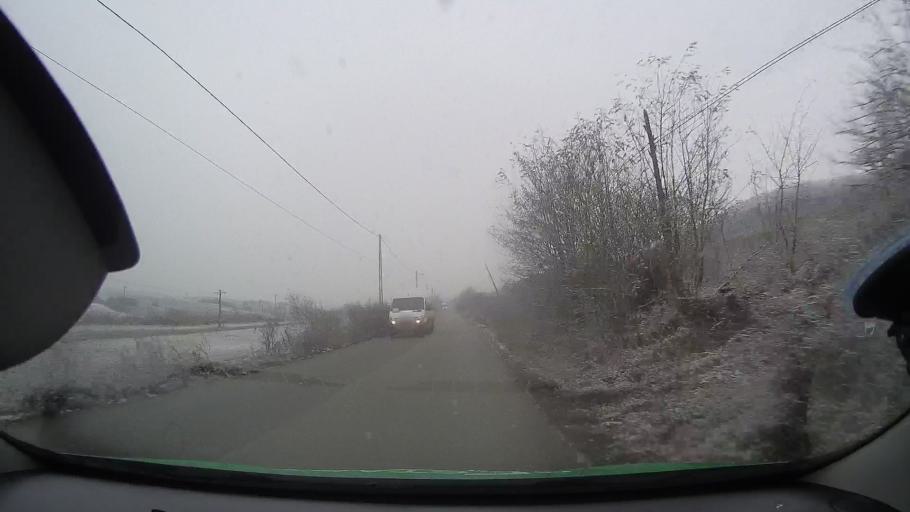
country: RO
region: Alba
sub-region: Comuna Noslac
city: Noslac
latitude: 46.3408
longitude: 23.9474
